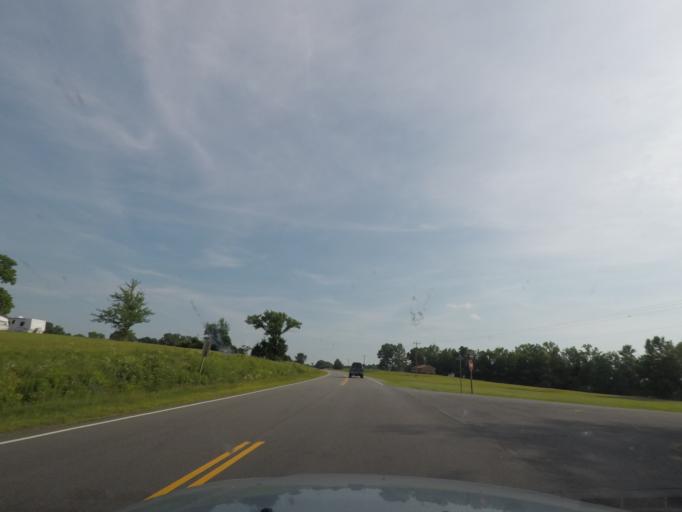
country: US
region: Virginia
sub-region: Mecklenburg County
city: Clarksville
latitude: 36.7494
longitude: -78.6357
